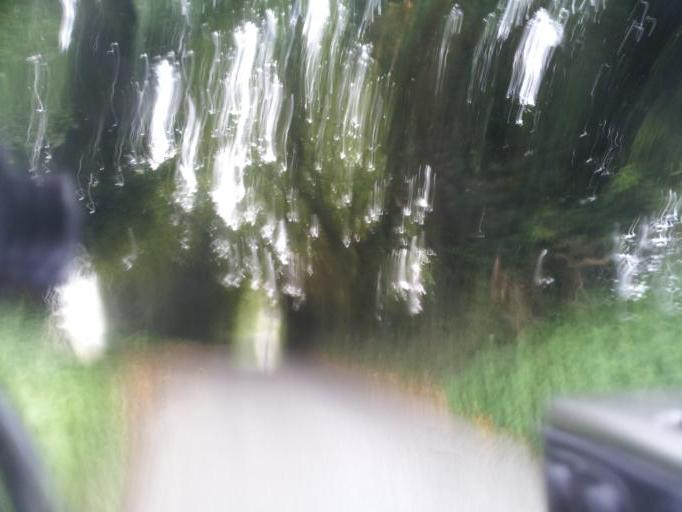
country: GB
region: England
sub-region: Kent
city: Newington
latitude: 51.3583
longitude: 0.6800
